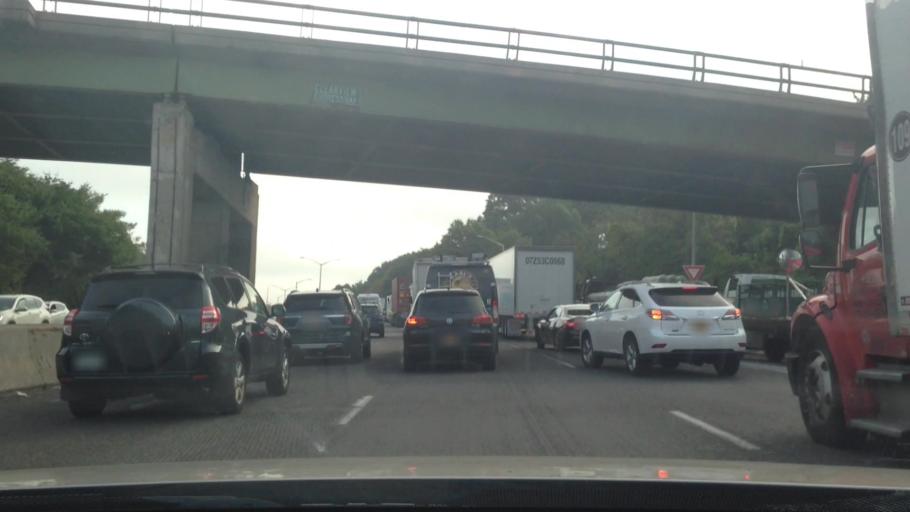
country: US
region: New York
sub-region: Nassau County
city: Bellerose Terrace
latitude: 40.7438
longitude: -73.7727
